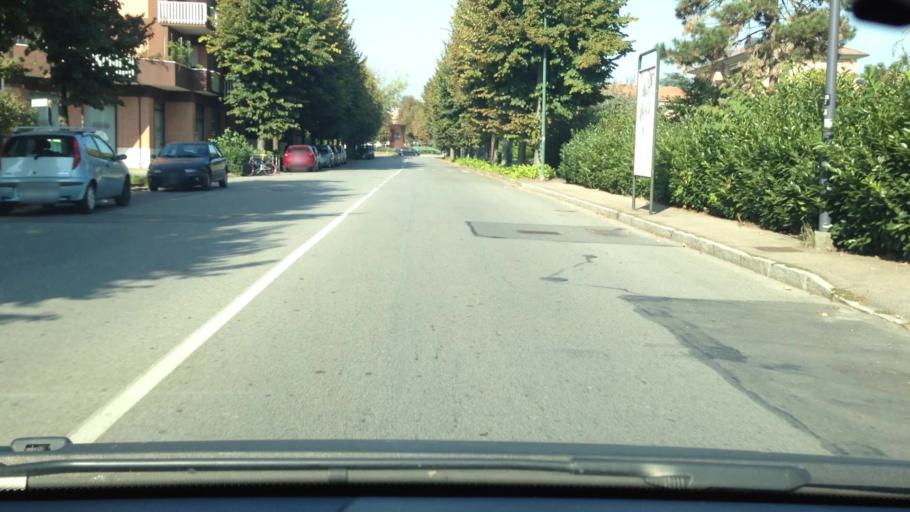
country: IT
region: Piedmont
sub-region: Provincia di Asti
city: Asti
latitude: 44.9065
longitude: 8.1930
